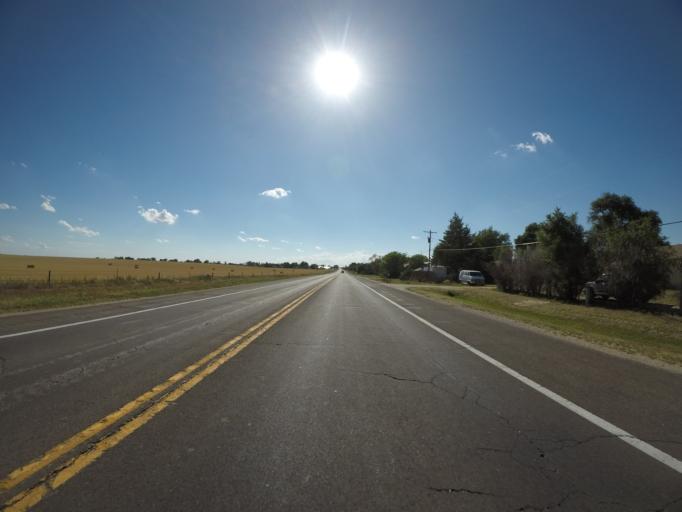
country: US
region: Colorado
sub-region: Logan County
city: Sterling
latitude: 40.6238
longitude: -103.2894
